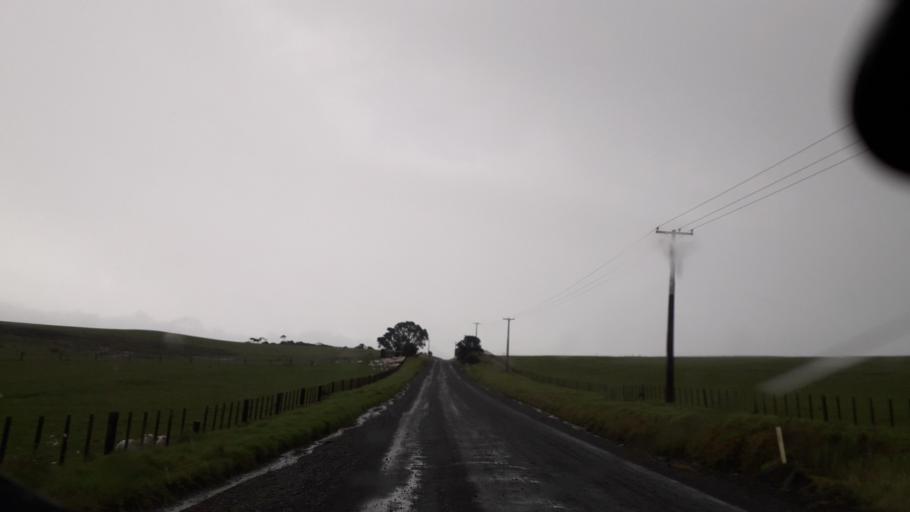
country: NZ
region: Northland
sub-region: Far North District
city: Kerikeri
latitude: -35.1360
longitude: 174.0223
